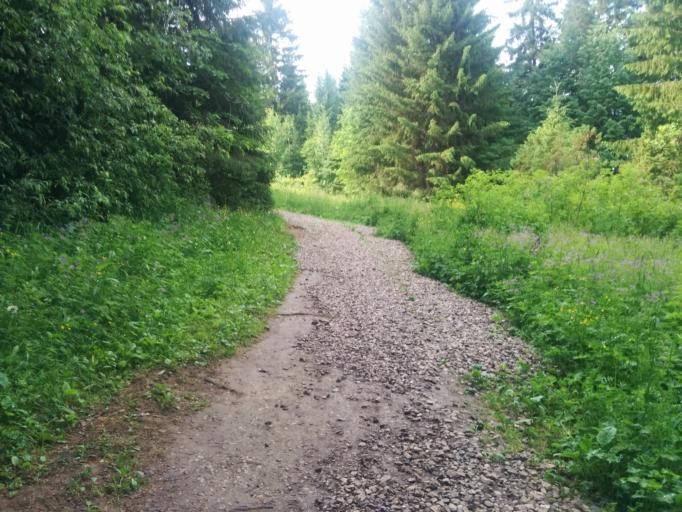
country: RU
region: Perm
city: Polazna
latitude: 58.2633
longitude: 56.2652
